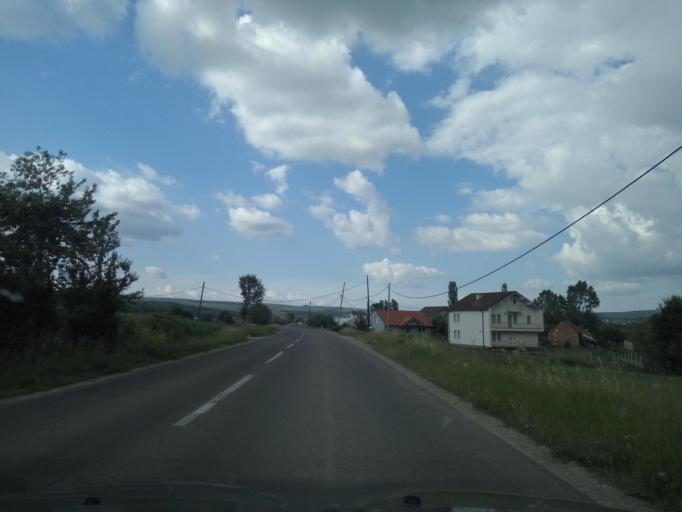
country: XK
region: Pec
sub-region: Komuna e Pejes
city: Kosuriq
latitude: 42.4685
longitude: 20.5046
